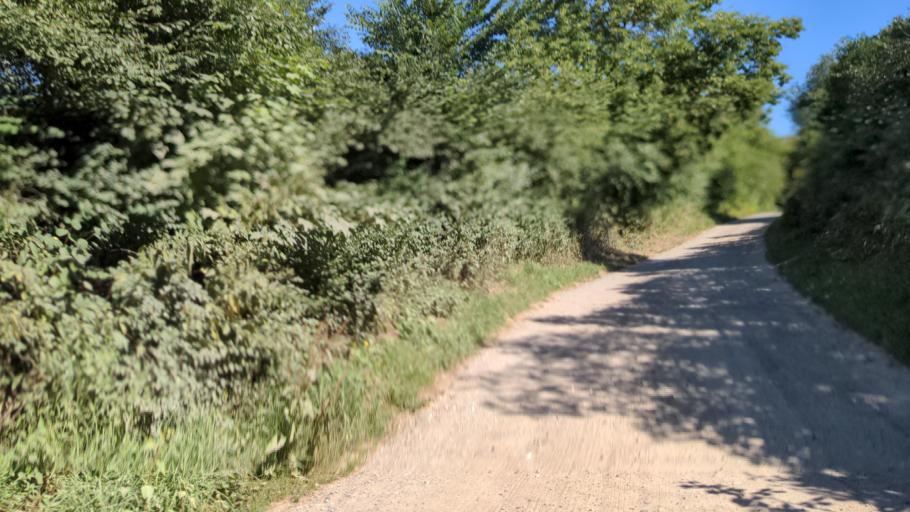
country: DE
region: Mecklenburg-Vorpommern
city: Klutz
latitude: 53.9853
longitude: 11.1719
